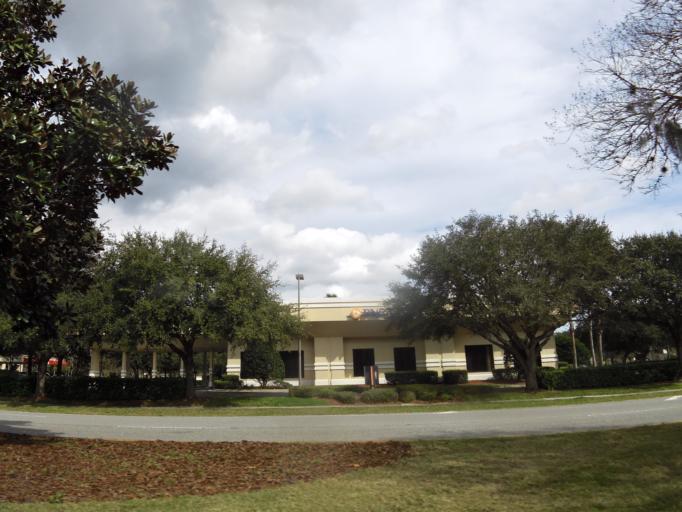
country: US
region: Florida
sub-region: Flagler County
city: Palm Coast
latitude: 29.5492
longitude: -81.2362
